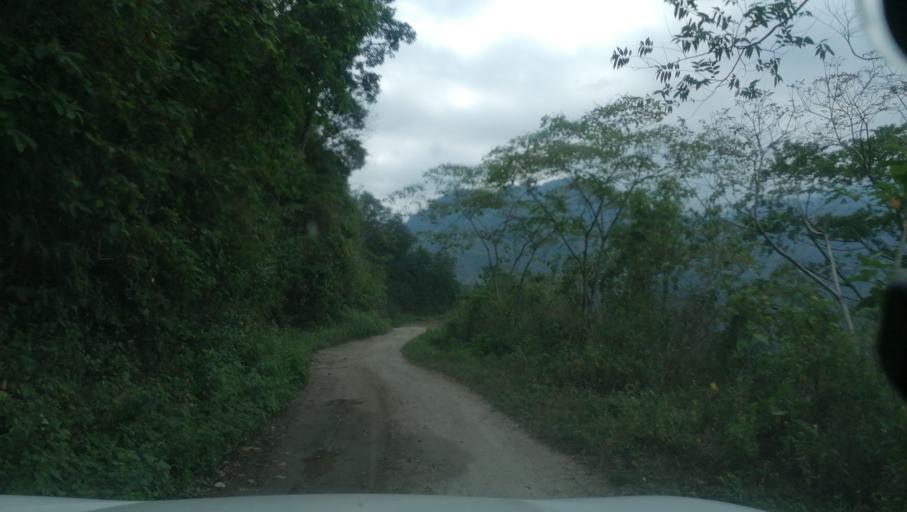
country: MX
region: Chiapas
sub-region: Cacahoatan
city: Benito Juarez
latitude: 15.1651
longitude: -92.1709
